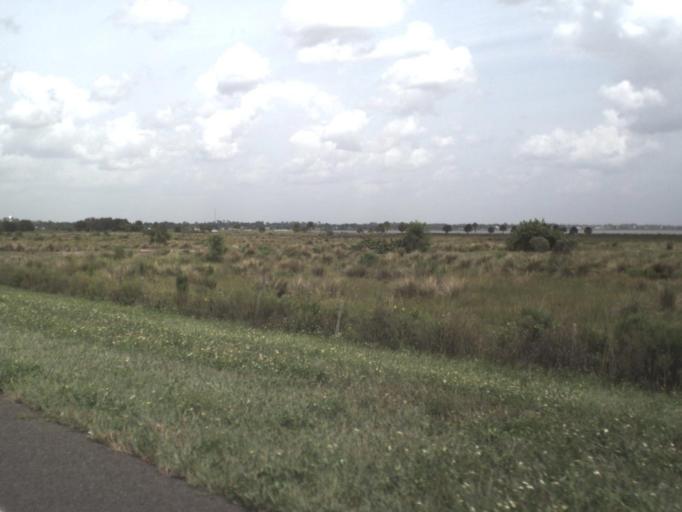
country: US
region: Florida
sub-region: Polk County
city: Crooked Lake Park
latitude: 27.8082
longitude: -81.5972
